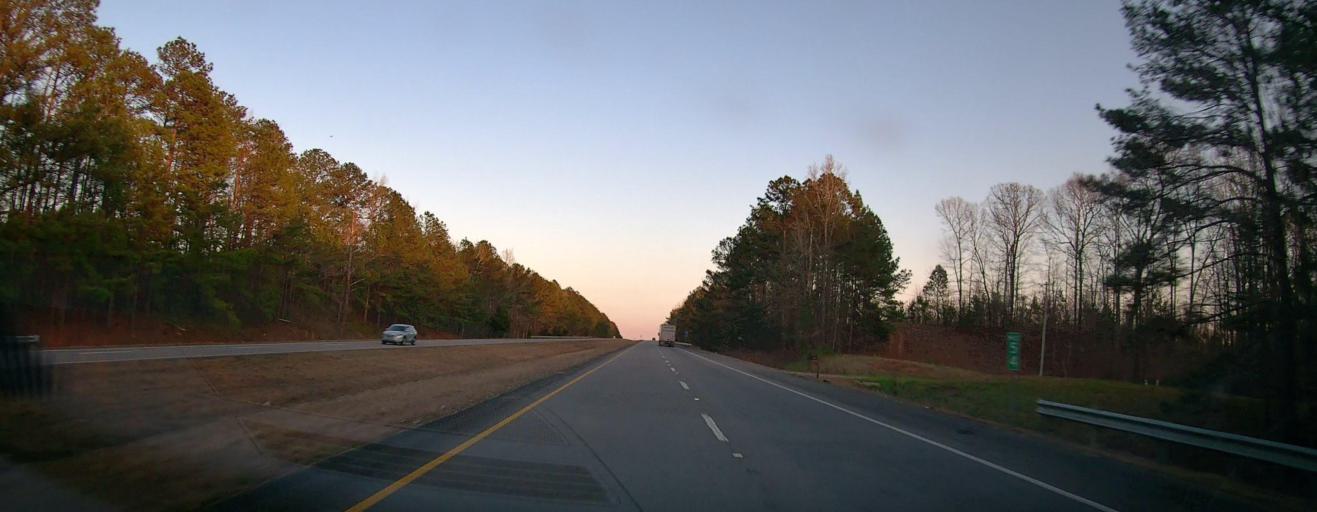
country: US
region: Alabama
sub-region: Coosa County
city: Goodwater
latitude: 33.0470
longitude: -86.1385
